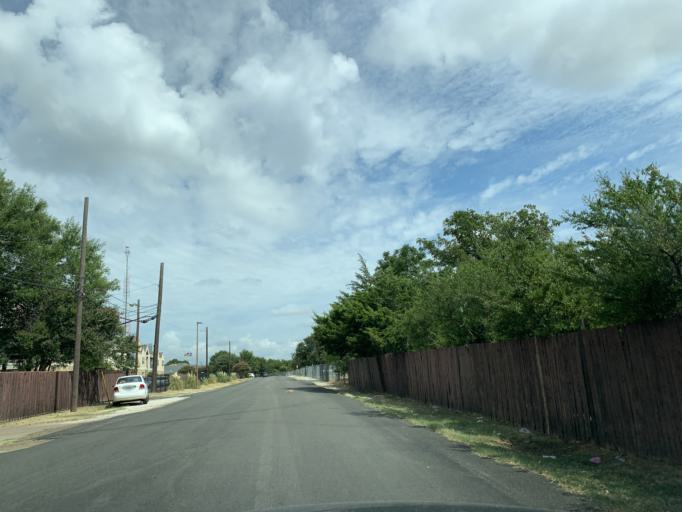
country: US
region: Texas
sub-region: Dallas County
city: Cockrell Hill
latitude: 32.7599
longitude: -96.8671
